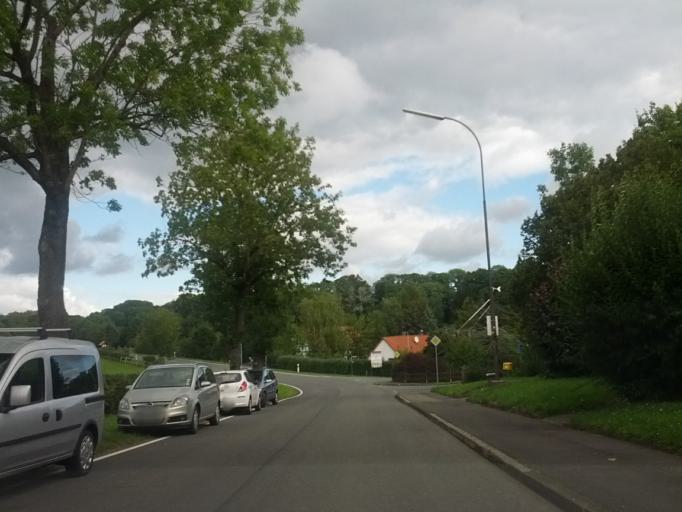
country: DE
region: Hesse
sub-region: Regierungsbezirk Kassel
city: Herleshausen
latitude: 51.0523
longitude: 10.1189
